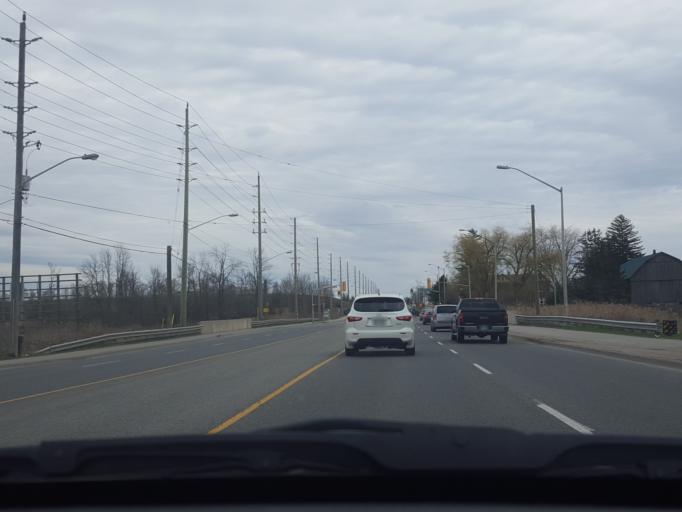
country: CA
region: Ontario
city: Ajax
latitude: 43.8480
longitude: -79.0003
